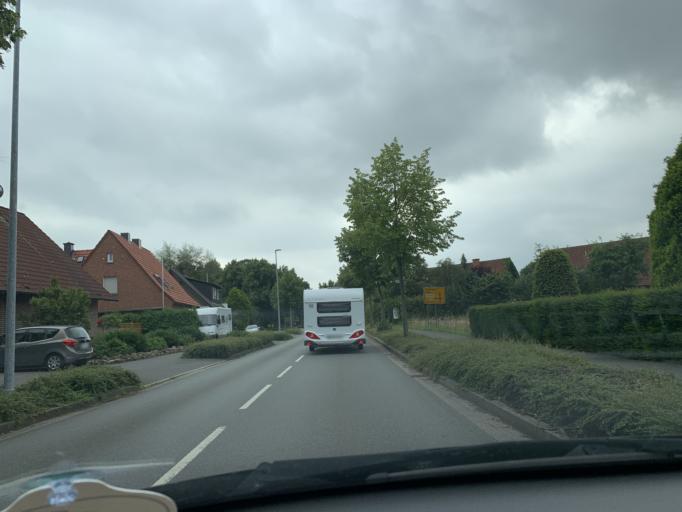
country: DE
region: North Rhine-Westphalia
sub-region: Regierungsbezirk Munster
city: Ostbevern
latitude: 52.0433
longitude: 7.8395
